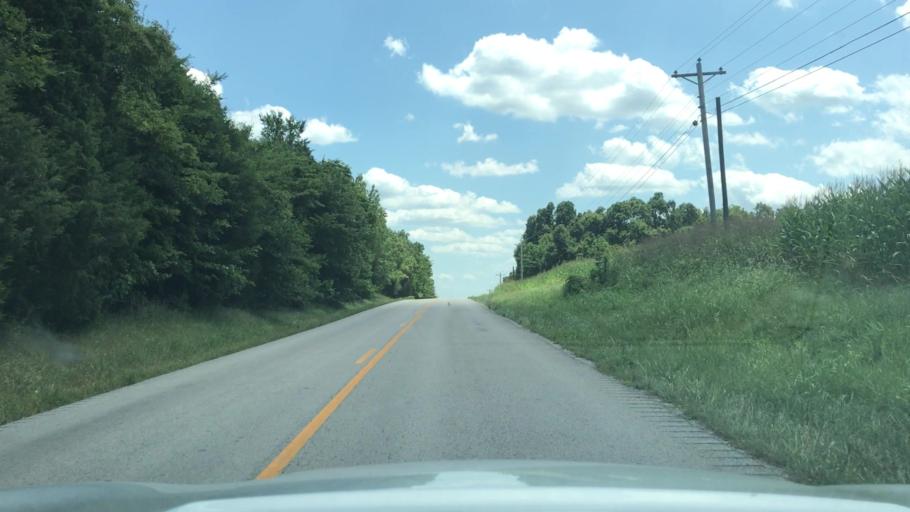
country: US
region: Kentucky
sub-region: Christian County
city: Hopkinsville
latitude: 36.9922
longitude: -87.3625
